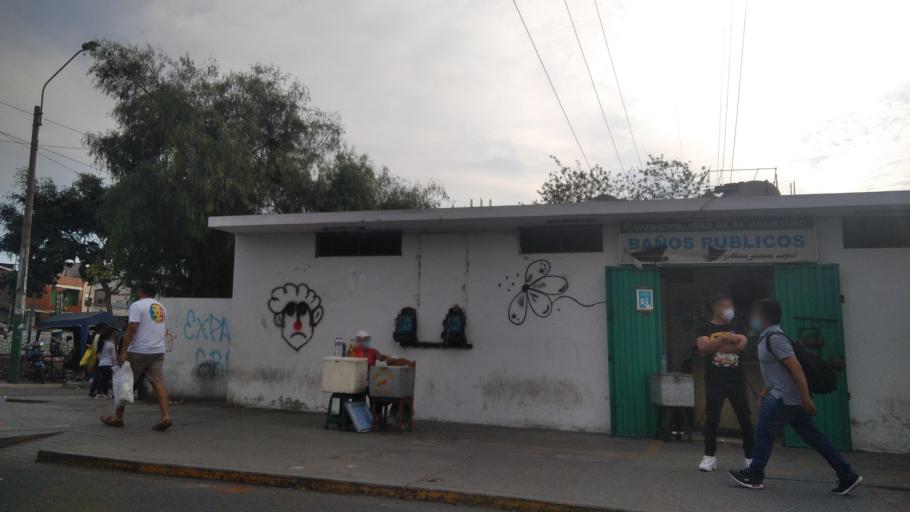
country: PE
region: Lima
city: Lima
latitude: -12.0286
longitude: -77.0008
